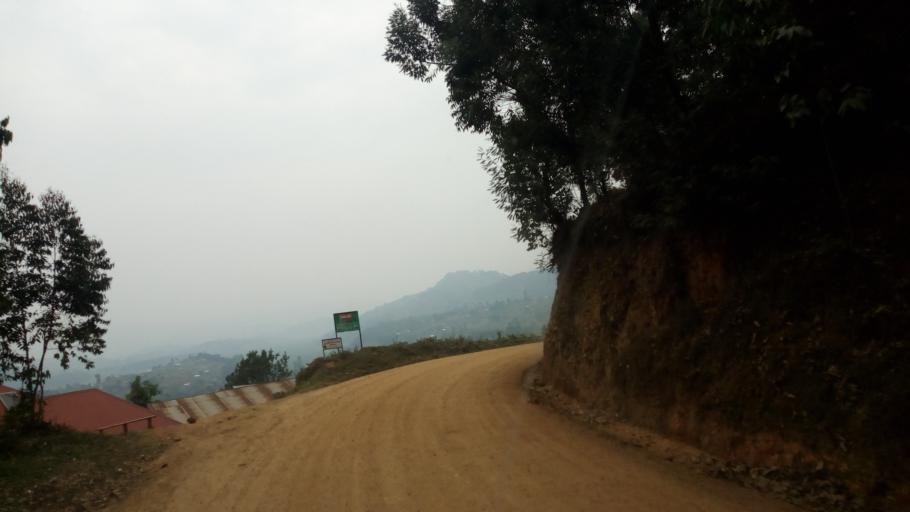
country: UG
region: Western Region
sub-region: Kanungu District
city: Kanungu
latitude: -1.1027
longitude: 29.8561
